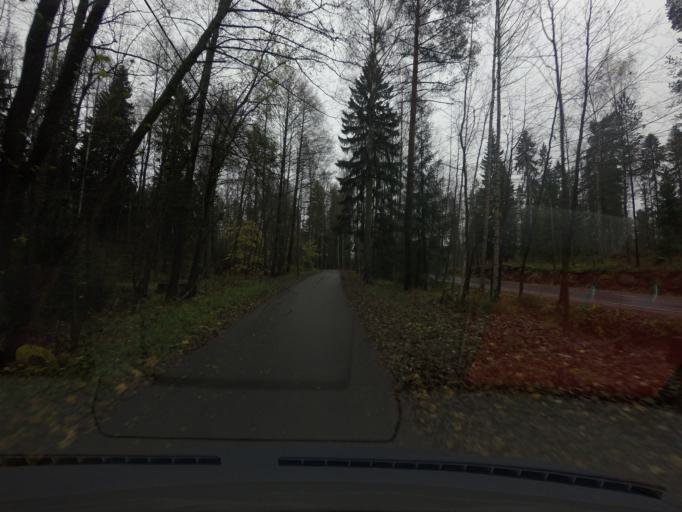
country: FI
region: Uusimaa
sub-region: Helsinki
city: Kilo
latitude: 60.2298
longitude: 24.7551
